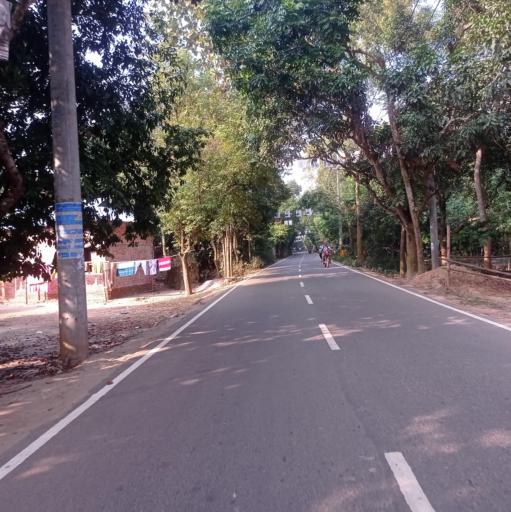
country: BD
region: Dhaka
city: Bhairab Bazar
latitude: 24.0511
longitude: 90.8352
